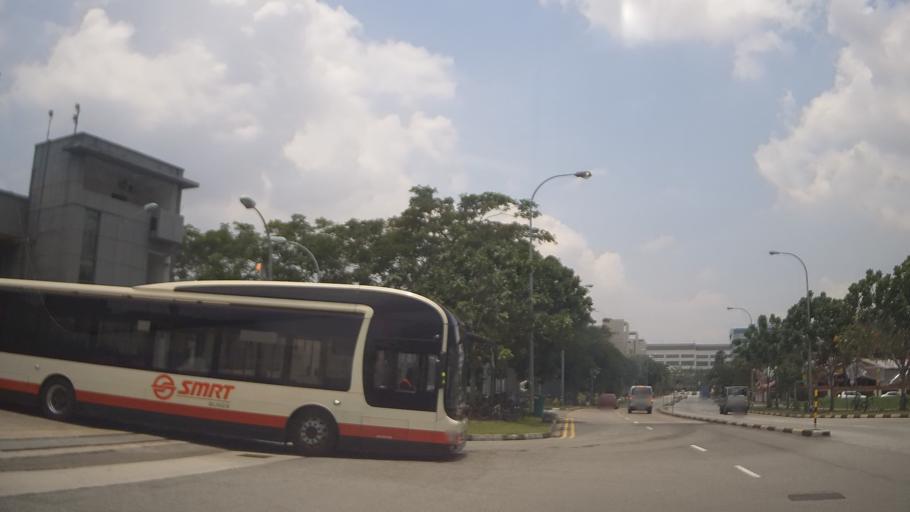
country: MY
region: Johor
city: Johor Bahru
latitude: 1.4496
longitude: 103.7959
